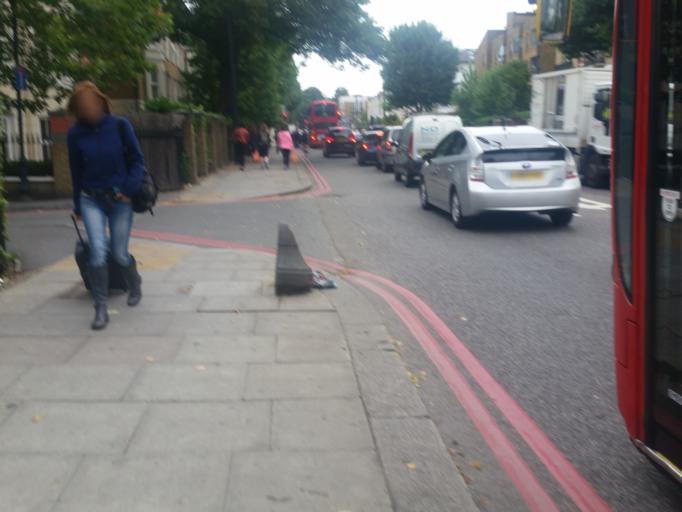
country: GB
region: England
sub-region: Greater London
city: Holloway
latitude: 51.5472
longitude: -0.1315
